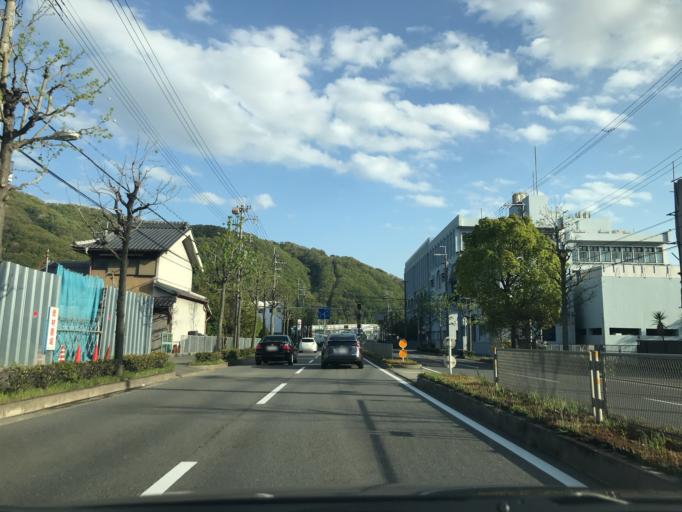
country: JP
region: Osaka
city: Ikeda
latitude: 34.8432
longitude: 135.4237
